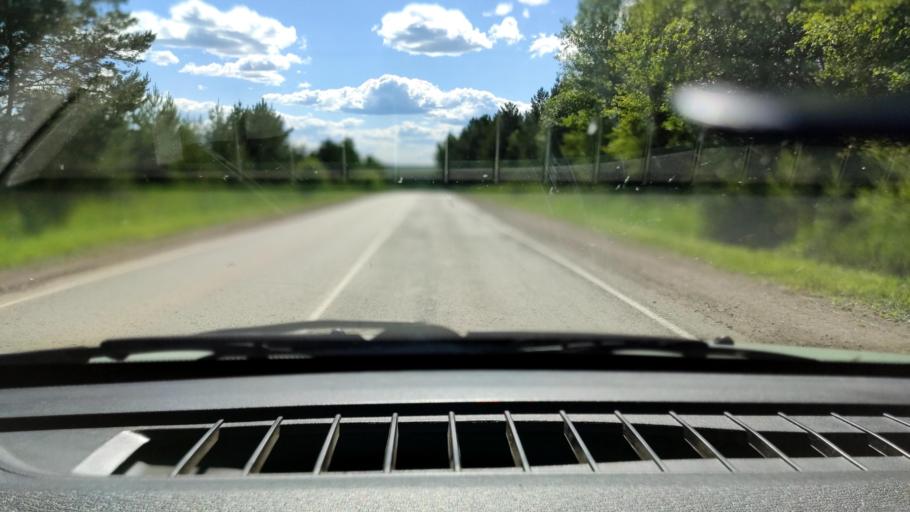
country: RU
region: Perm
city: Kukushtan
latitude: 57.3141
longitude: 56.5545
